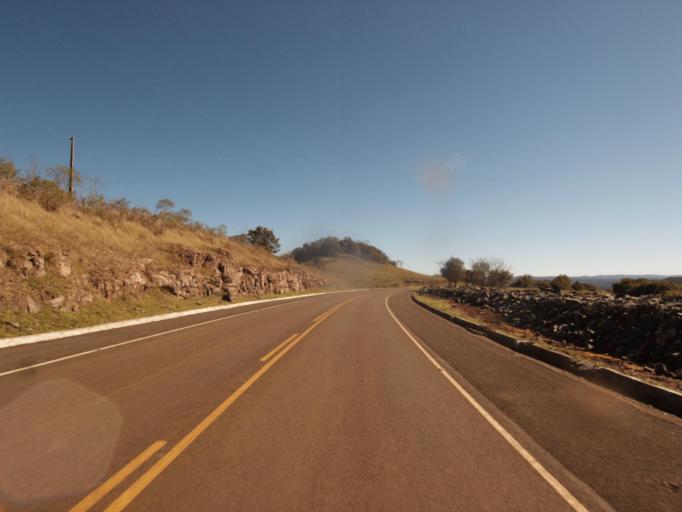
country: AR
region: Misiones
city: Bernardo de Irigoyen
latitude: -26.6147
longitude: -53.7062
